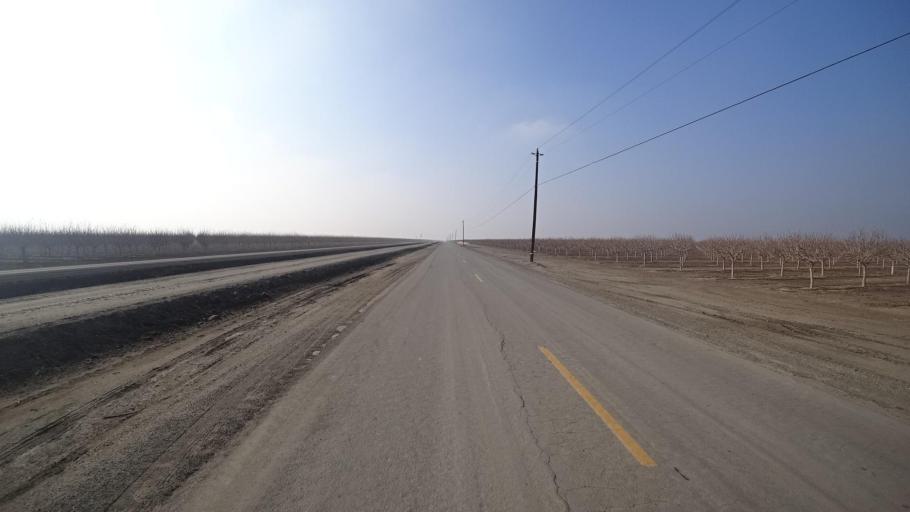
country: US
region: California
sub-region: Kern County
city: Greenfield
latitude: 35.1514
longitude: -119.0599
